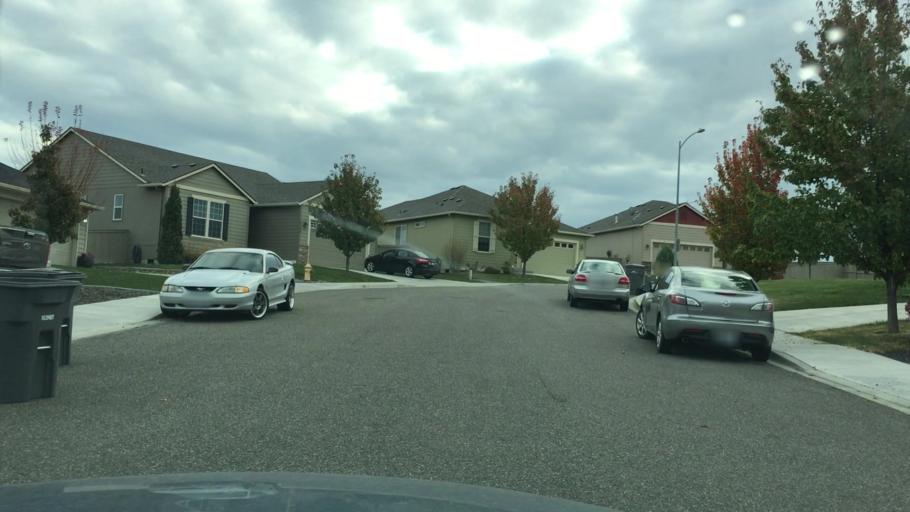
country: US
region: Washington
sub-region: Franklin County
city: West Pasco
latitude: 46.1893
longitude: -119.1982
